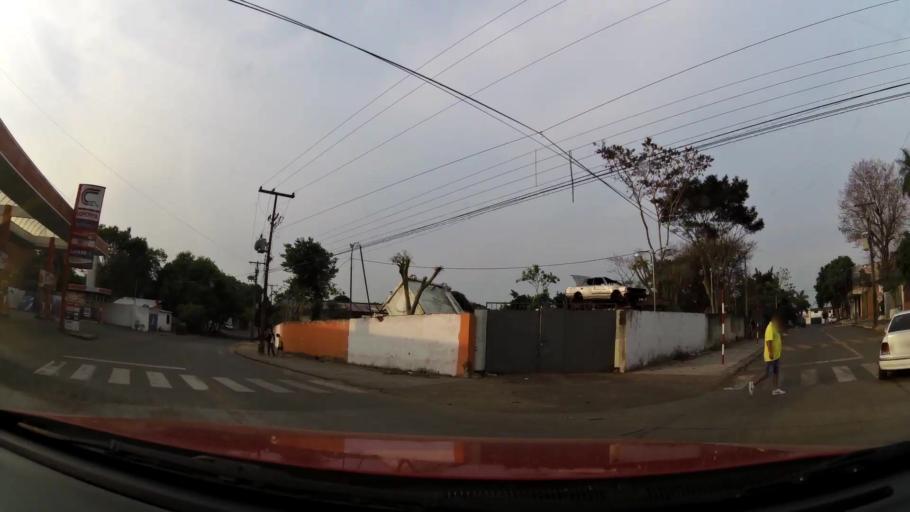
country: PY
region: Central
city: Lambare
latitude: -25.3303
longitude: -57.5746
